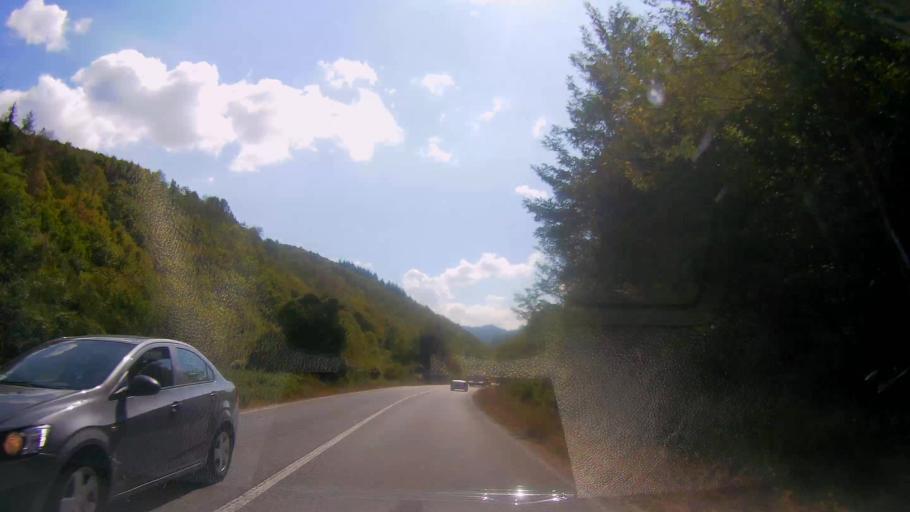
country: BG
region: Stara Zagora
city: Gurkovo
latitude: 42.7453
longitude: 25.7093
